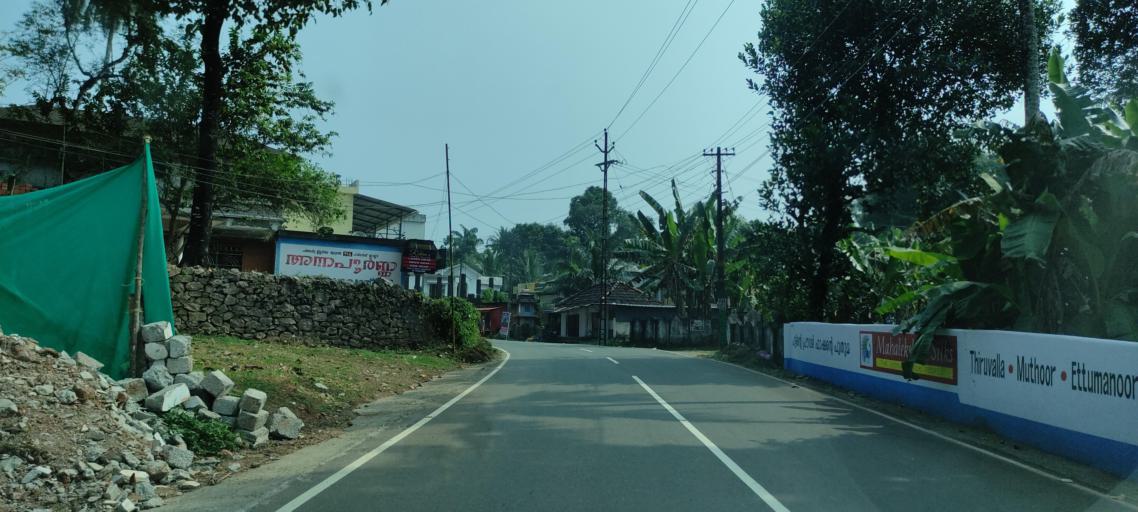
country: IN
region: Kerala
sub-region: Pattanamtitta
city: Adur
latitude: 9.2370
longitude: 76.6957
